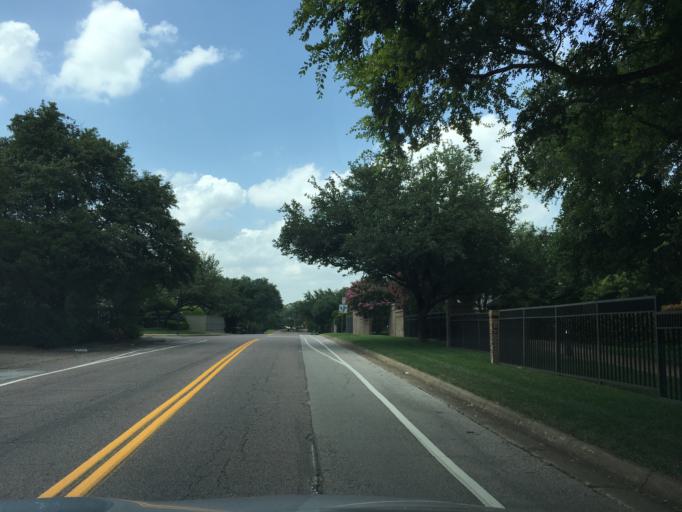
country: US
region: Texas
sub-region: Dallas County
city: University Park
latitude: 32.8781
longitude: -96.7787
